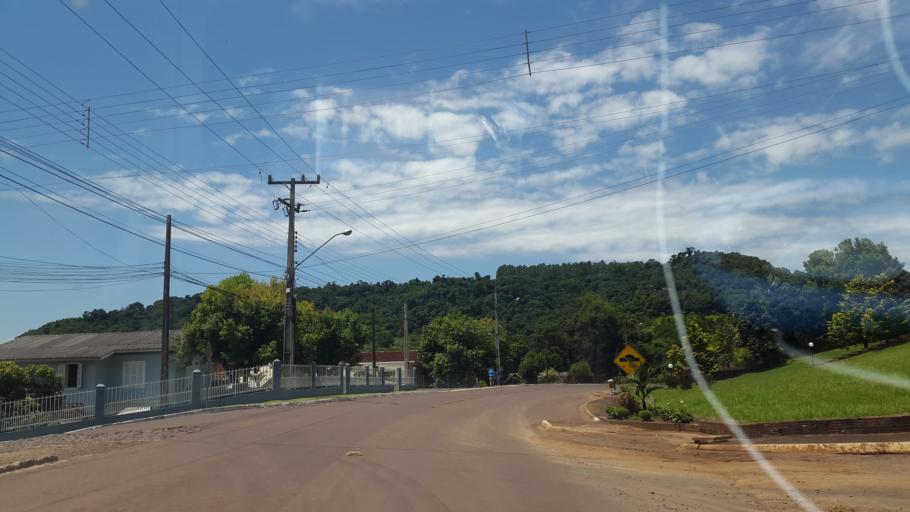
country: BR
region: Rio Grande do Sul
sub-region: Frederico Westphalen
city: Frederico Westphalen
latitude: -27.0697
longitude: -53.4284
